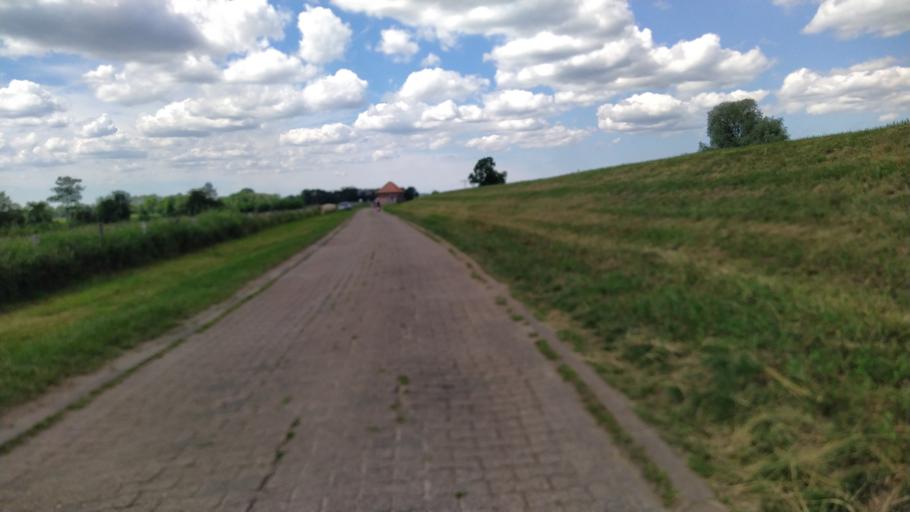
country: DE
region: Lower Saxony
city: Estorf
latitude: 53.5738
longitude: 9.1679
